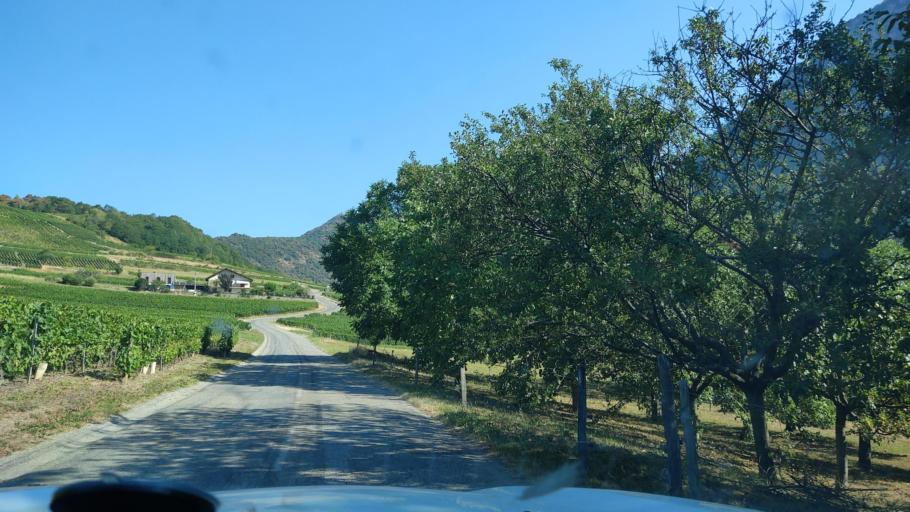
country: FR
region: Rhone-Alpes
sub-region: Departement de la Savoie
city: Les Marches
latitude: 45.5278
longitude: 6.0072
